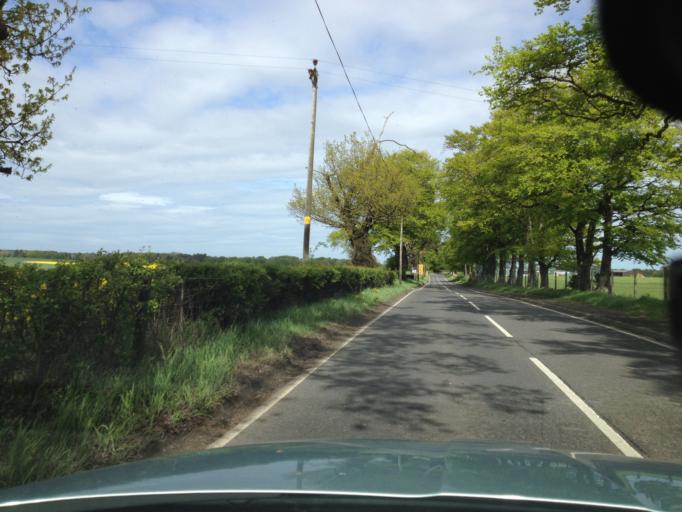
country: GB
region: Scotland
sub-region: West Lothian
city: West Calder
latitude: 55.8706
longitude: -3.5672
